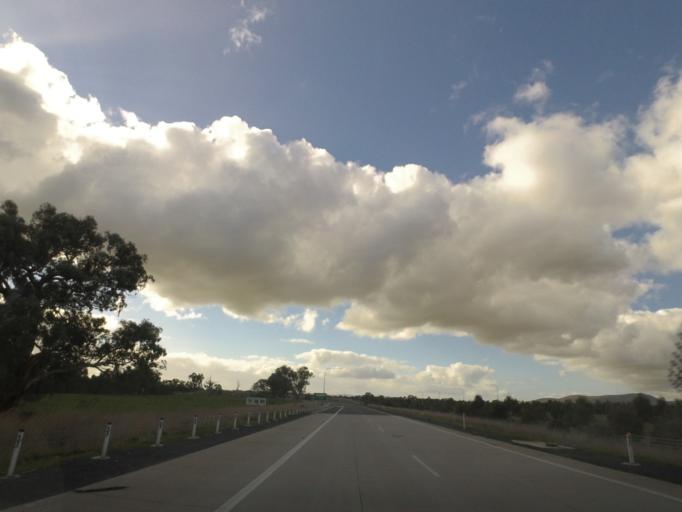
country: AU
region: New South Wales
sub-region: Greater Hume Shire
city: Holbrook
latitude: -35.7397
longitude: 147.3033
